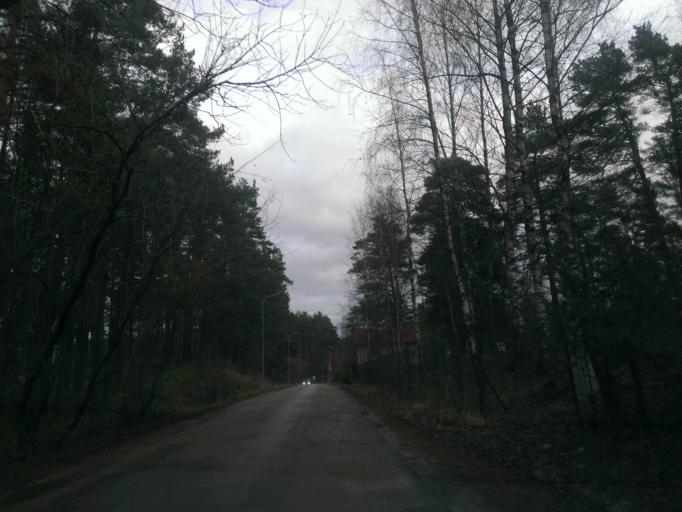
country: LV
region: Riga
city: Bergi
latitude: 57.0089
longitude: 24.3242
